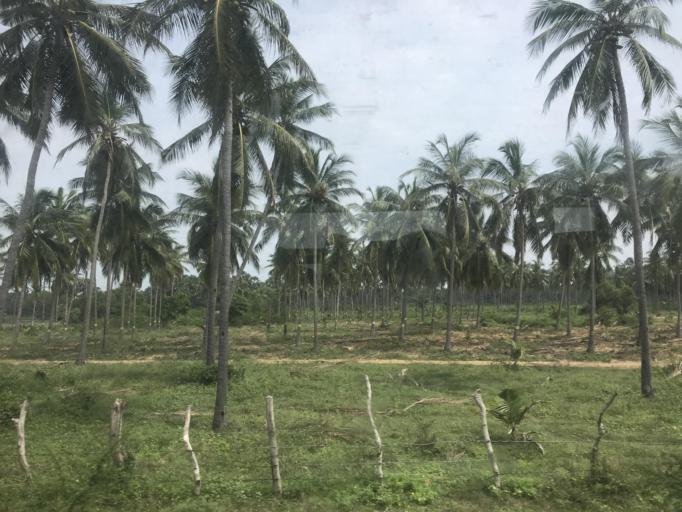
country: LK
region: Northern Province
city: Kilinochchi
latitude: 9.5846
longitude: 80.3508
